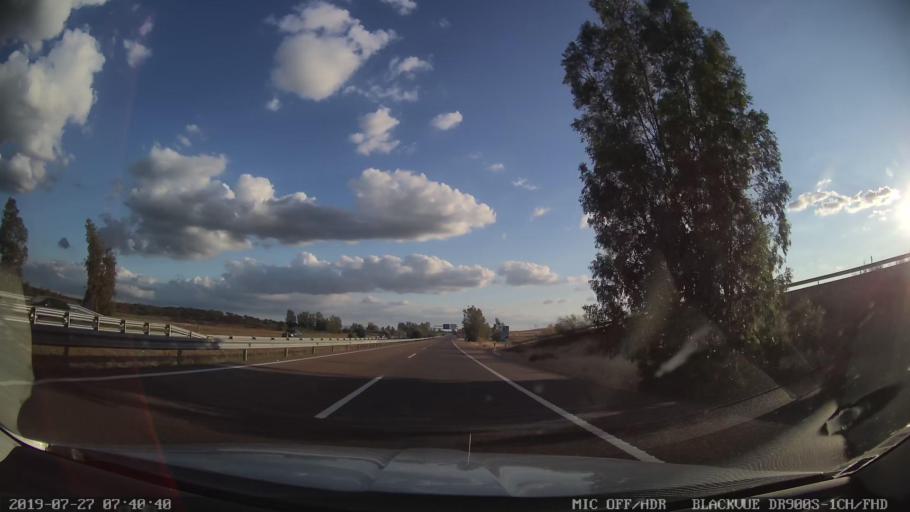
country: ES
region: Extremadura
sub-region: Provincia de Badajoz
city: Santa Amalia
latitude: 39.0422
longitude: -6.0619
